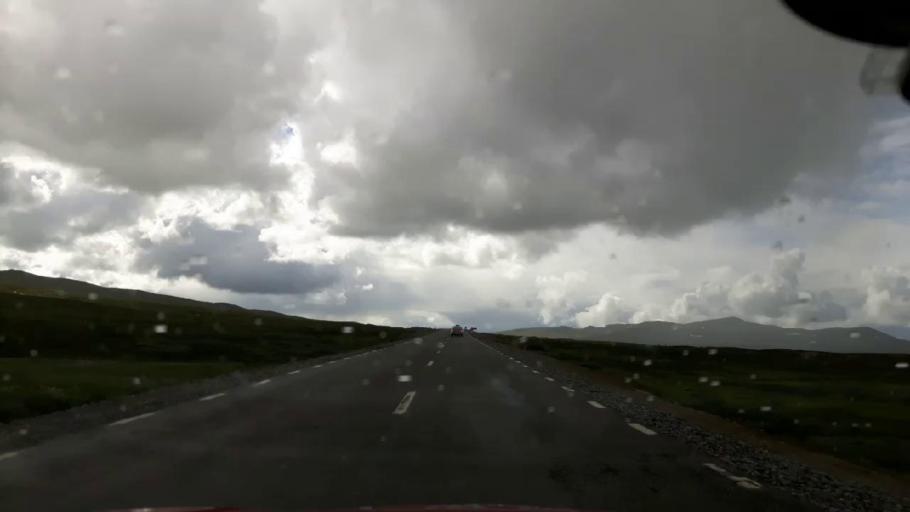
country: NO
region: Nordland
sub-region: Hattfjelldal
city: Hattfjelldal
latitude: 65.1004
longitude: 14.4677
